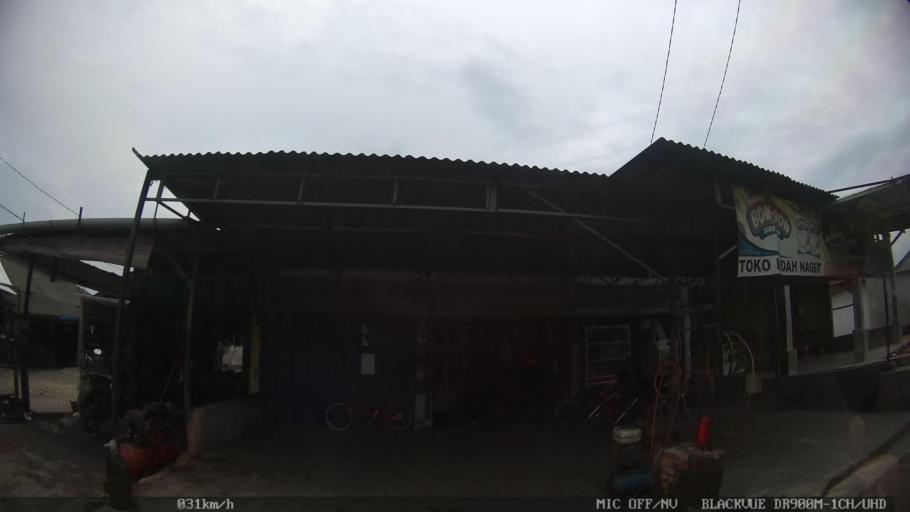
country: ID
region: North Sumatra
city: Binjai
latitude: 3.6247
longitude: 98.5555
